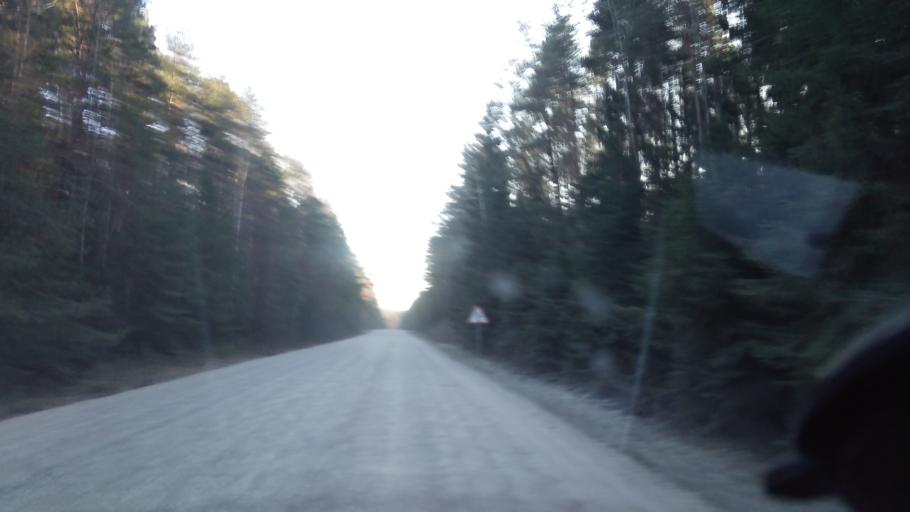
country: LT
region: Alytaus apskritis
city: Druskininkai
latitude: 54.1463
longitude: 23.9407
